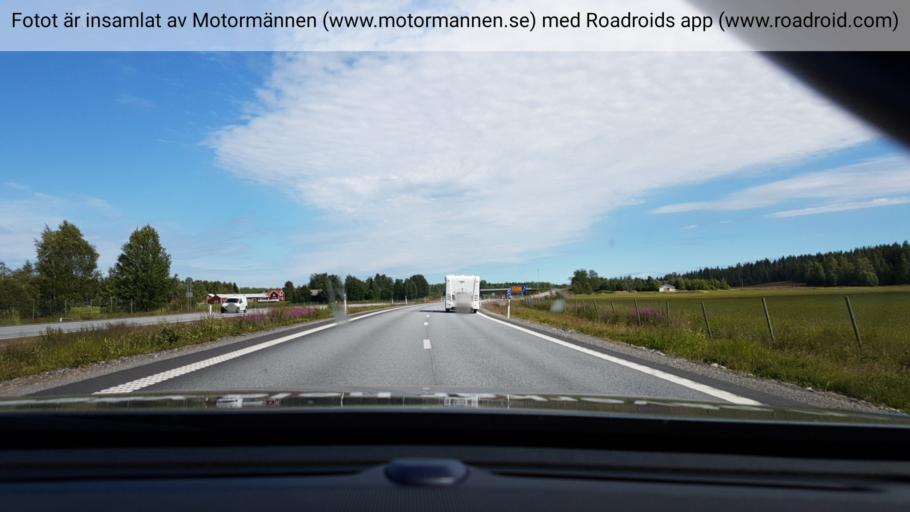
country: SE
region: Vaesterbotten
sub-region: Skelleftea Kommun
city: Kage
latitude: 64.8468
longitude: 20.9895
